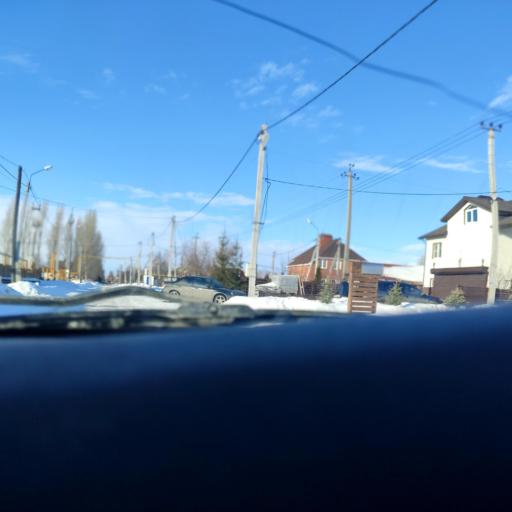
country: RU
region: Samara
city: Podstepki
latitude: 53.5110
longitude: 49.1644
